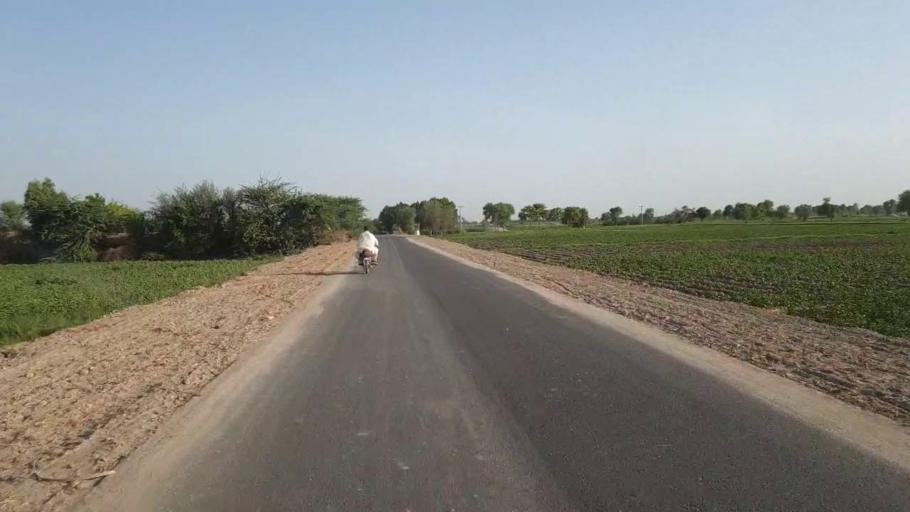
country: PK
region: Sindh
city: Jam Sahib
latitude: 26.3430
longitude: 68.5689
